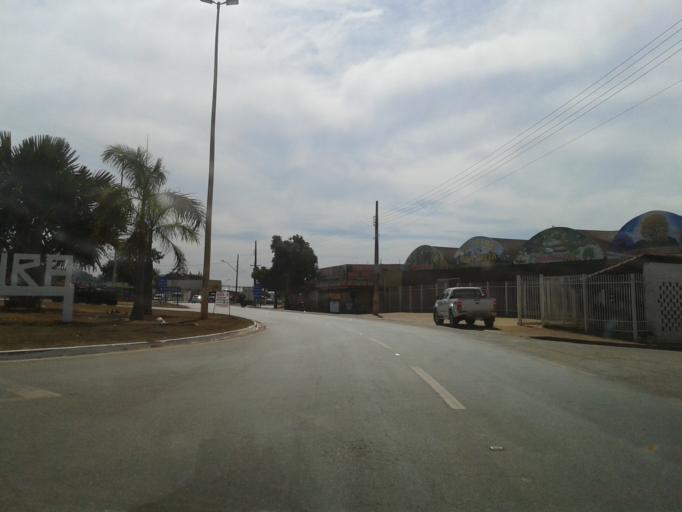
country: BR
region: Goias
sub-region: Goianira
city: Goianira
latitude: -16.5069
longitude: -49.4221
